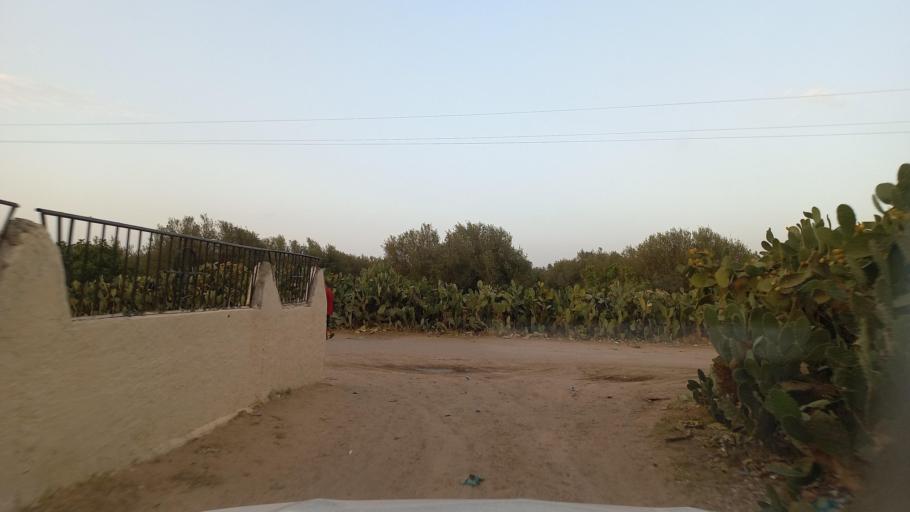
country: TN
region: Al Qasrayn
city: Kasserine
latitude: 35.2684
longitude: 9.0585
